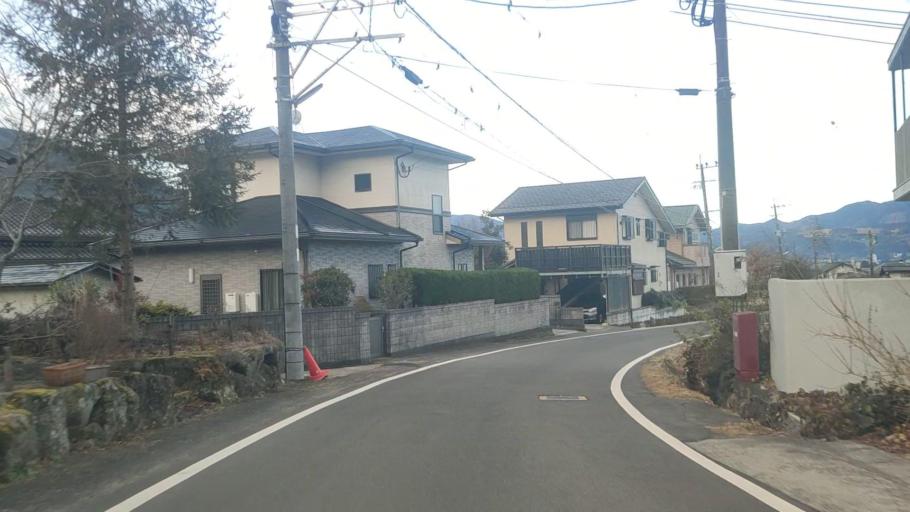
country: JP
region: Oita
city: Beppu
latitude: 33.2614
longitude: 131.3684
